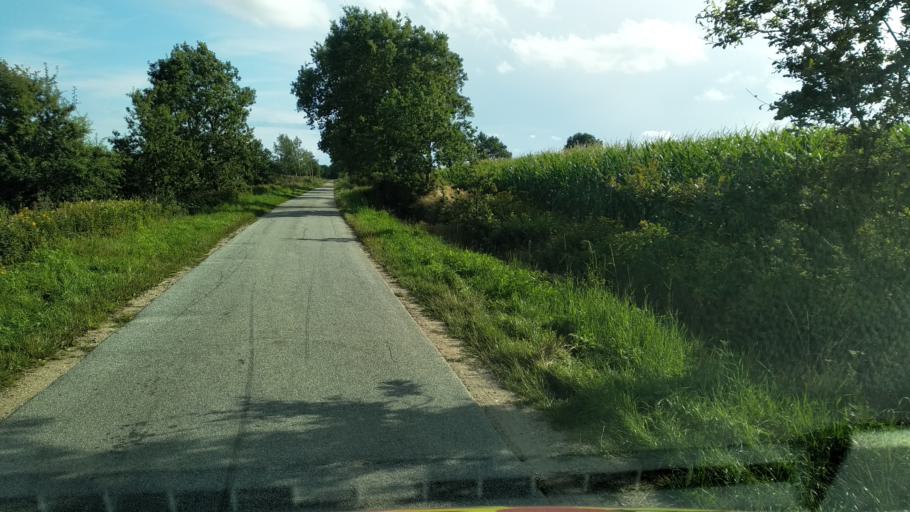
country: DE
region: Schleswig-Holstein
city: Gross Rheide
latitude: 54.4323
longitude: 9.4289
